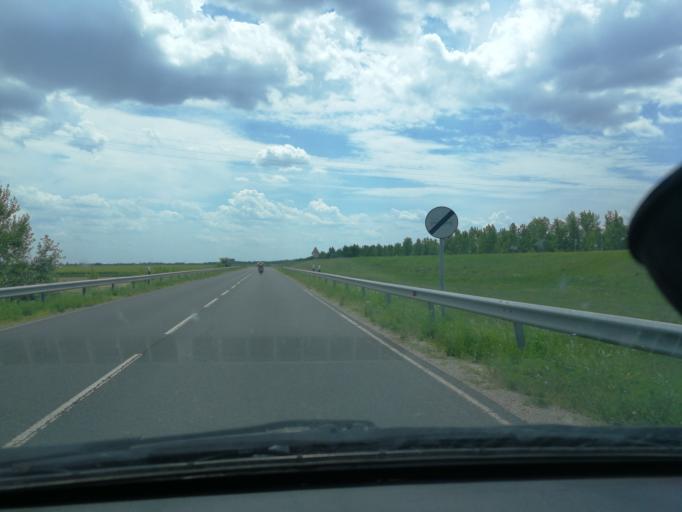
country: HU
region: Bacs-Kiskun
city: Harta
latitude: 46.6841
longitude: 19.0162
